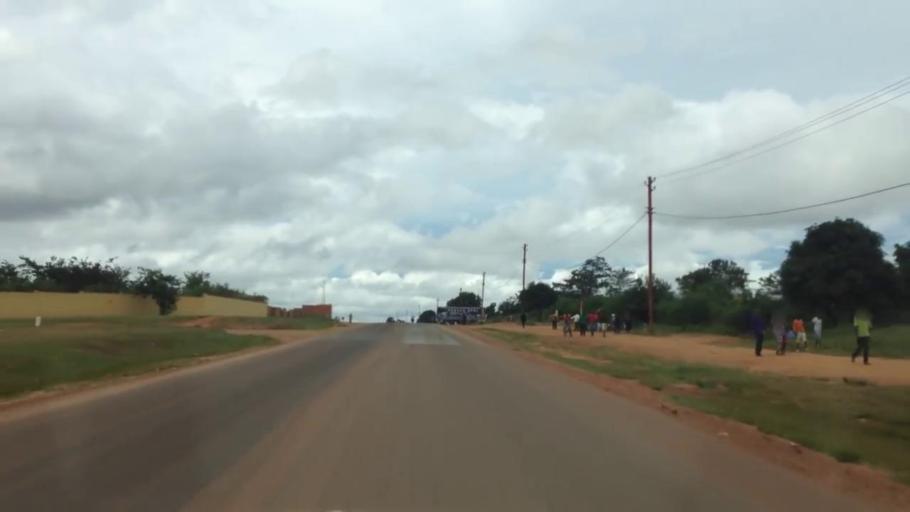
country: CD
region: Katanga
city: Kolwezi
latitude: -10.7275
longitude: 25.5092
